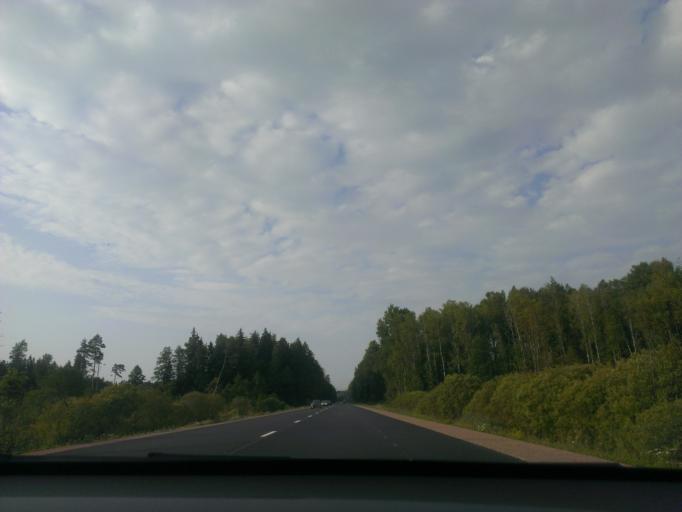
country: LV
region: Lecava
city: Iecava
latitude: 56.7049
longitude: 24.2452
